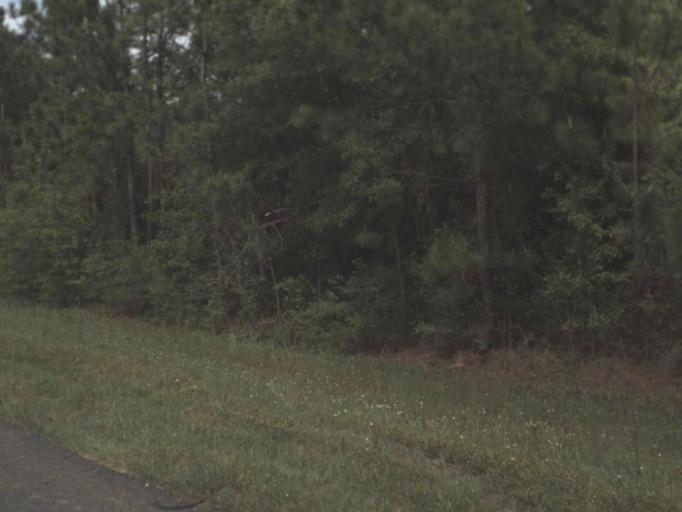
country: US
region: Florida
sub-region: Escambia County
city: Molino
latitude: 30.7340
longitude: -87.3490
